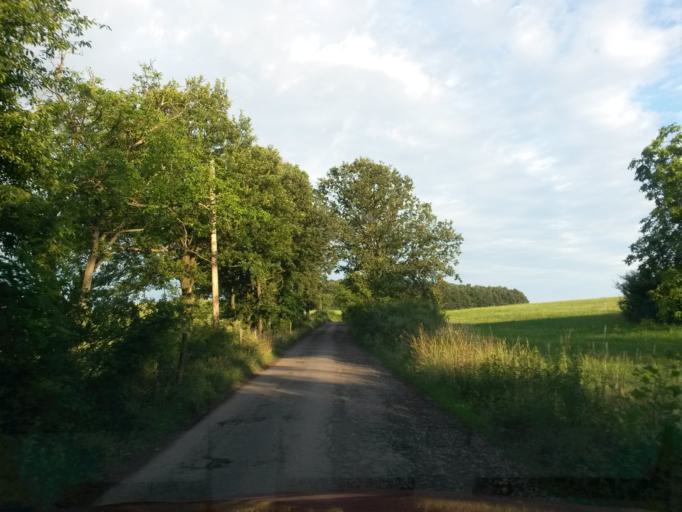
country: SK
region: Banskobystricky
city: Lucenec
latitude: 48.2872
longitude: 19.5027
